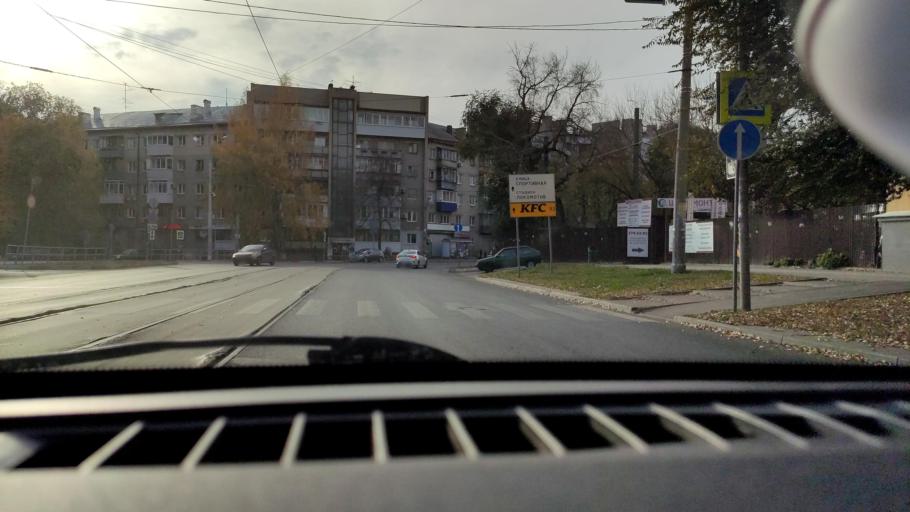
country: RU
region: Samara
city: Samara
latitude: 53.1880
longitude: 50.1257
